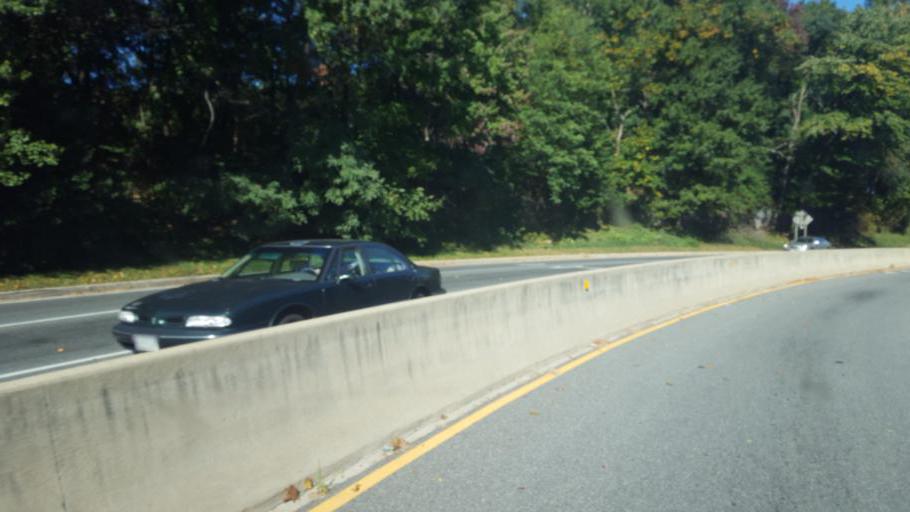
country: US
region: Maryland
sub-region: Montgomery County
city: Gaithersburg
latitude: 39.1483
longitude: -77.2185
